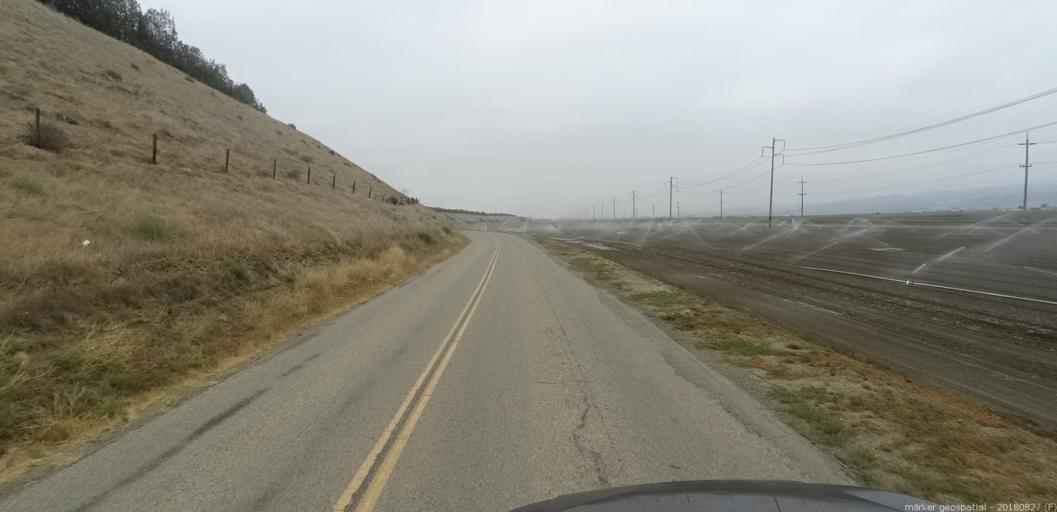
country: US
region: California
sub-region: Monterey County
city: King City
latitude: 36.2612
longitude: -121.1418
